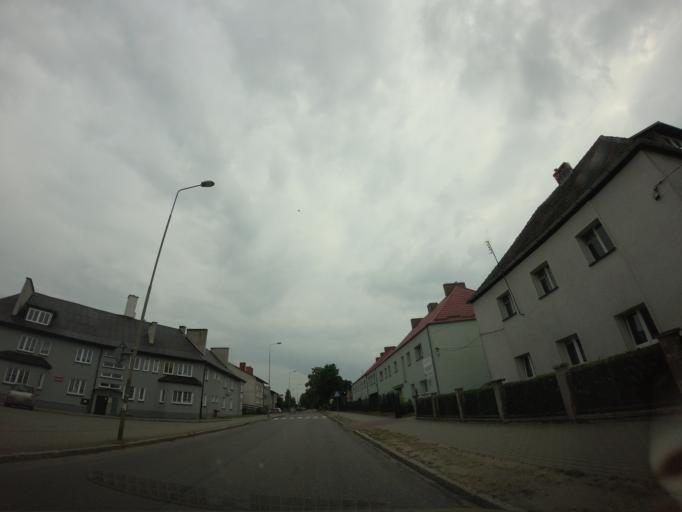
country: PL
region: West Pomeranian Voivodeship
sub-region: Powiat drawski
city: Czaplinek
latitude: 53.5550
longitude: 16.2327
